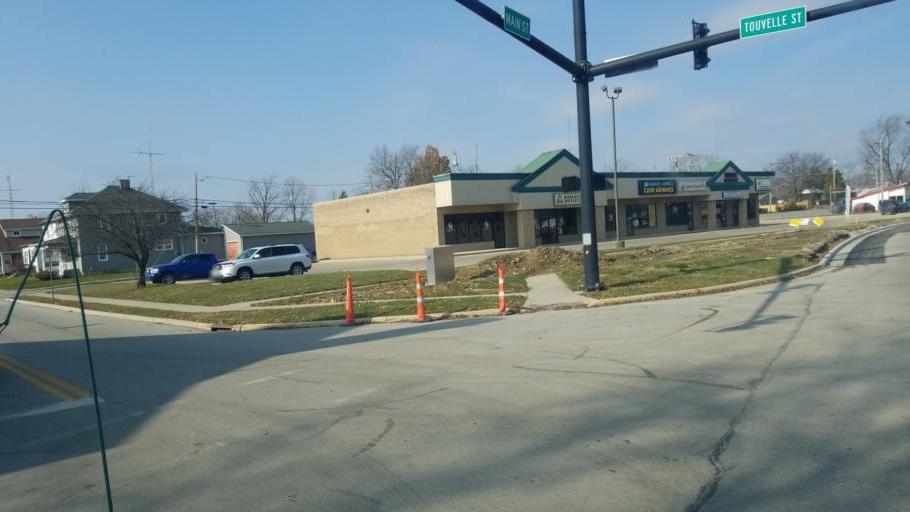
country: US
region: Ohio
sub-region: Mercer County
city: Celina
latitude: 40.5566
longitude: -84.5710
